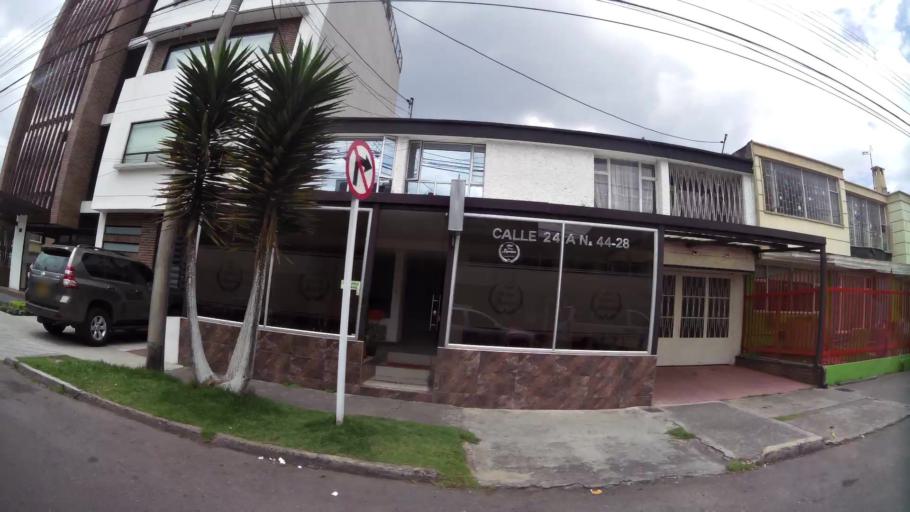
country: CO
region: Bogota D.C.
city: Bogota
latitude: 4.6336
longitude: -74.0940
